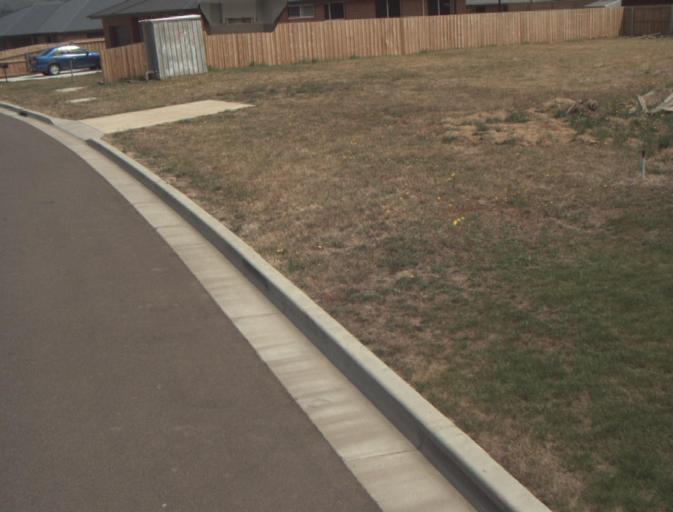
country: AU
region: Tasmania
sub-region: Launceston
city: Mayfield
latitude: -41.3820
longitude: 147.1128
